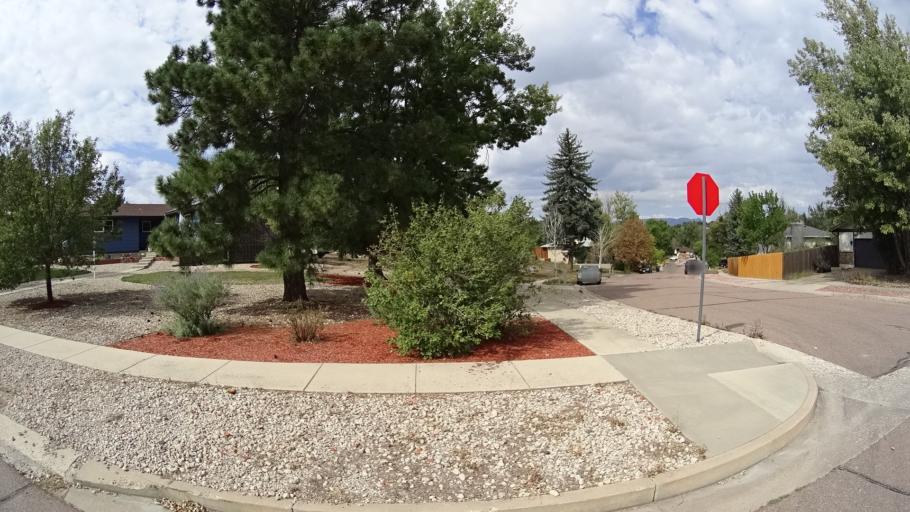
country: US
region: Colorado
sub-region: El Paso County
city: Cimarron Hills
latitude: 38.8591
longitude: -104.7300
